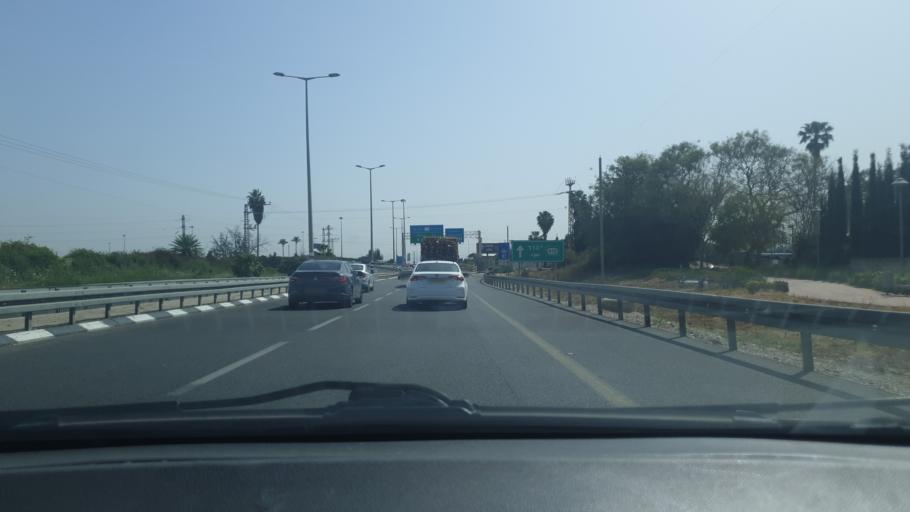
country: IL
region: Central District
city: Bet Dagan
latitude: 32.0054
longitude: 34.8311
